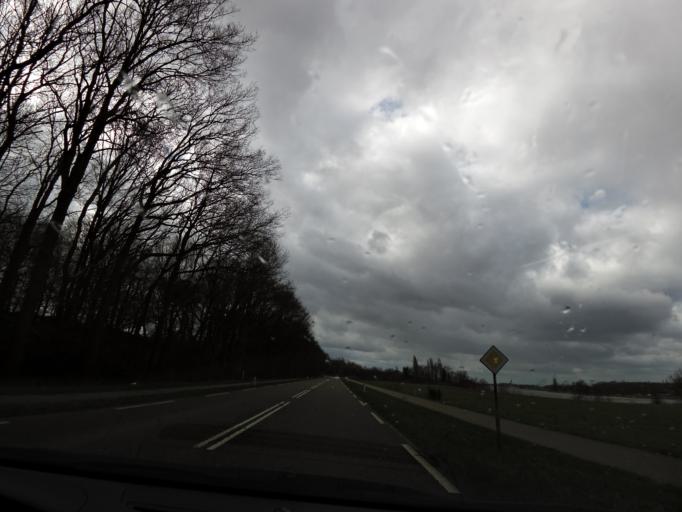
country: NL
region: Limburg
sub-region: Gemeente Beesel
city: Offenbeek
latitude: 51.2983
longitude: 6.0910
